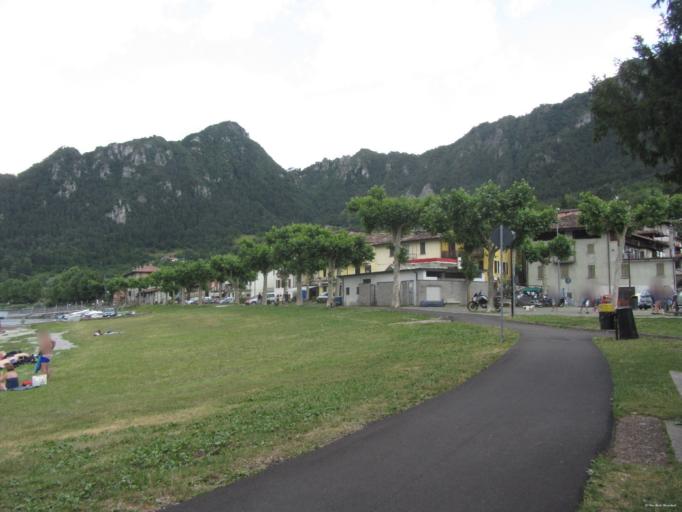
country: IT
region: Lombardy
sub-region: Provincia di Brescia
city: Crone
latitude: 45.7408
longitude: 10.4799
